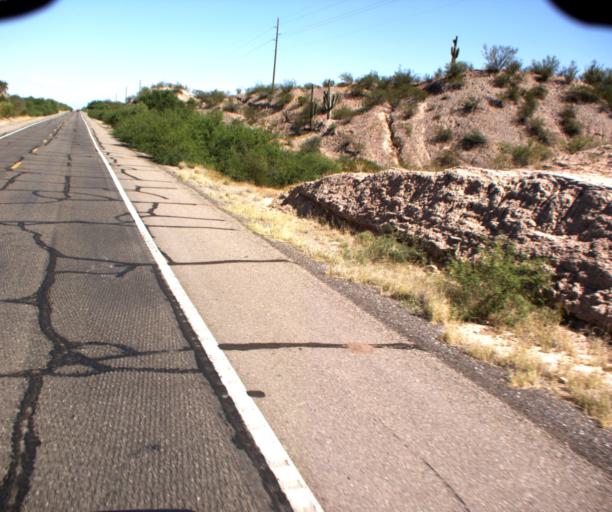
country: US
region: Arizona
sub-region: Pinal County
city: Mammoth
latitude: 32.7804
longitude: -110.6656
